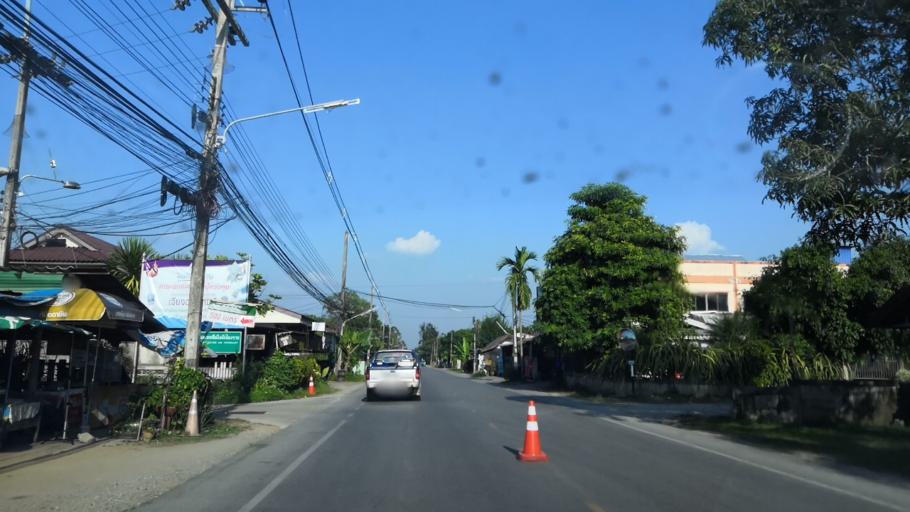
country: TH
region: Chiang Rai
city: Wiang Chai
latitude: 19.9357
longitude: 99.9055
